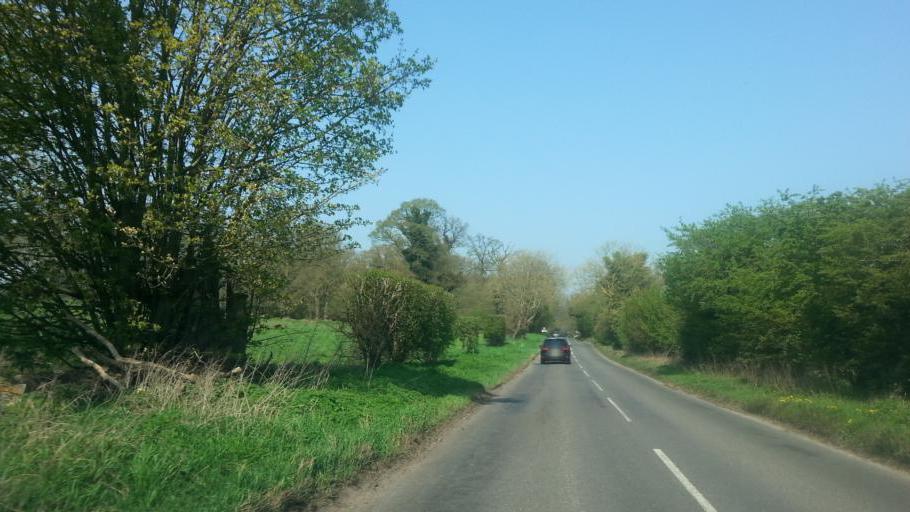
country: GB
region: England
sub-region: Suffolk
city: Thurston
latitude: 52.2427
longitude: 0.8212
